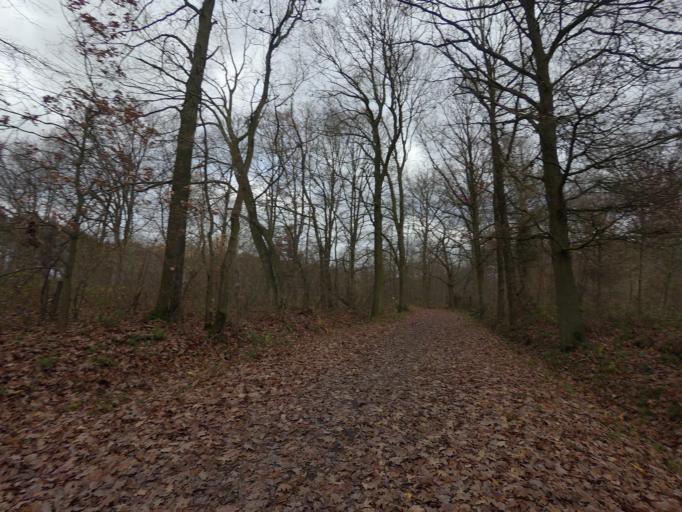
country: BE
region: Flanders
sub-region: Provincie Vlaams-Brabant
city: Haacht
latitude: 50.9544
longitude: 4.6164
